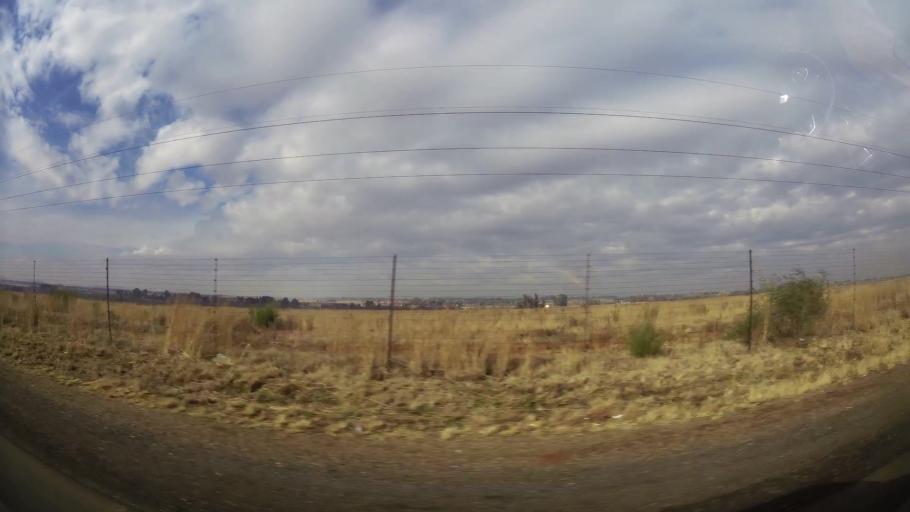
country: ZA
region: Gauteng
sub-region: Sedibeng District Municipality
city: Meyerton
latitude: -26.5578
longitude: 28.0469
